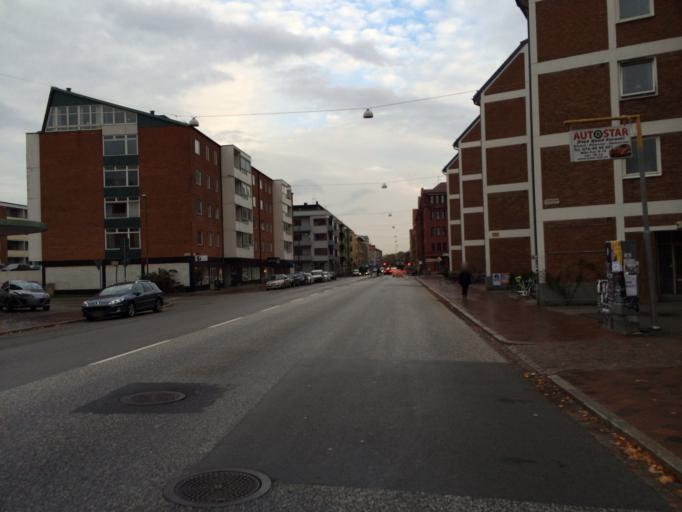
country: SE
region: Skane
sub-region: Malmo
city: Malmoe
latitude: 55.5944
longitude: 12.9835
